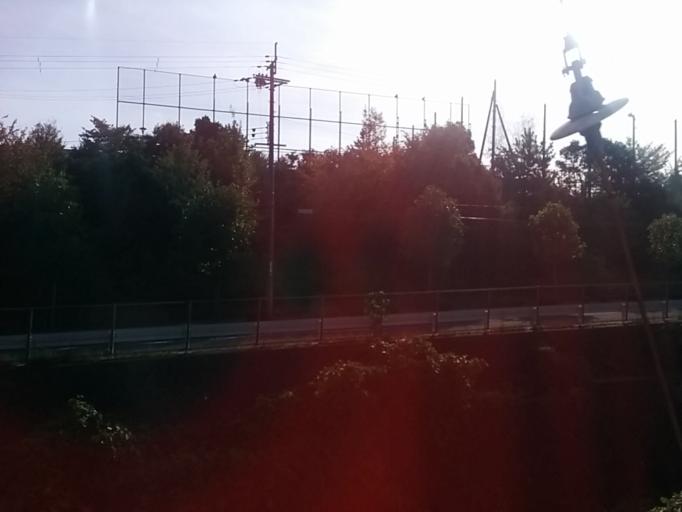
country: JP
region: Nara
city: Nara-shi
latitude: 34.7194
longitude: 135.7919
